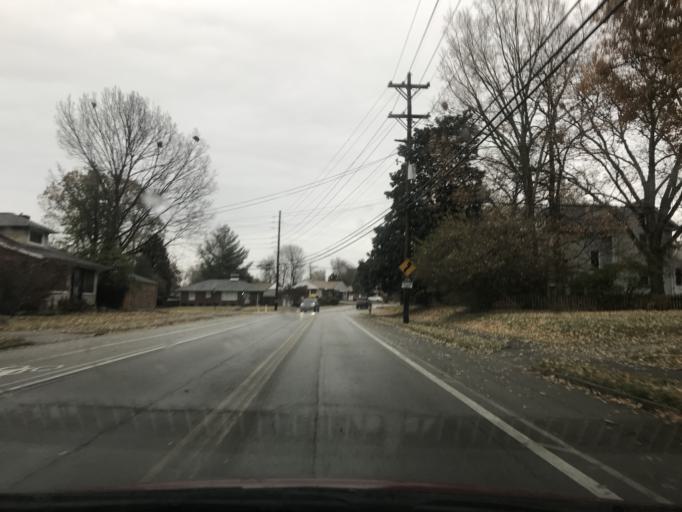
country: US
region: Kentucky
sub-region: Jefferson County
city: West Buechel
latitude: 38.2124
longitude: -85.6614
